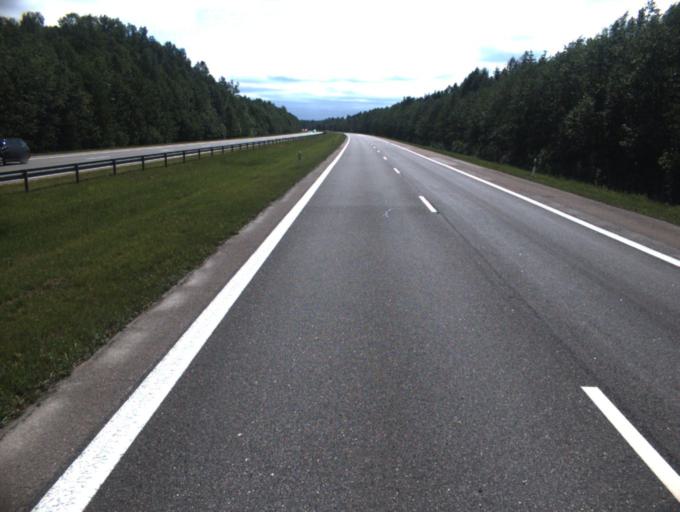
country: LT
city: Rietavas
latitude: 55.6524
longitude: 21.7915
